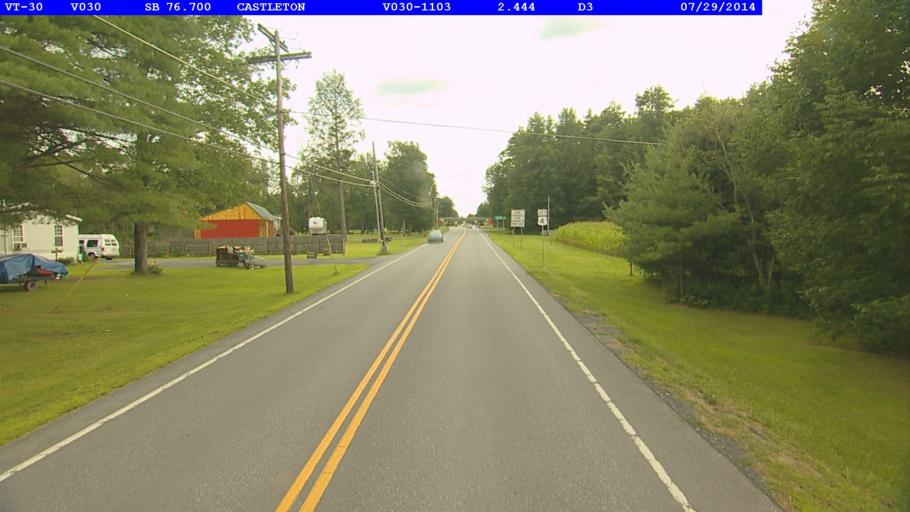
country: US
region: Vermont
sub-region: Rutland County
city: Castleton
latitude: 43.6218
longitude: -73.2055
